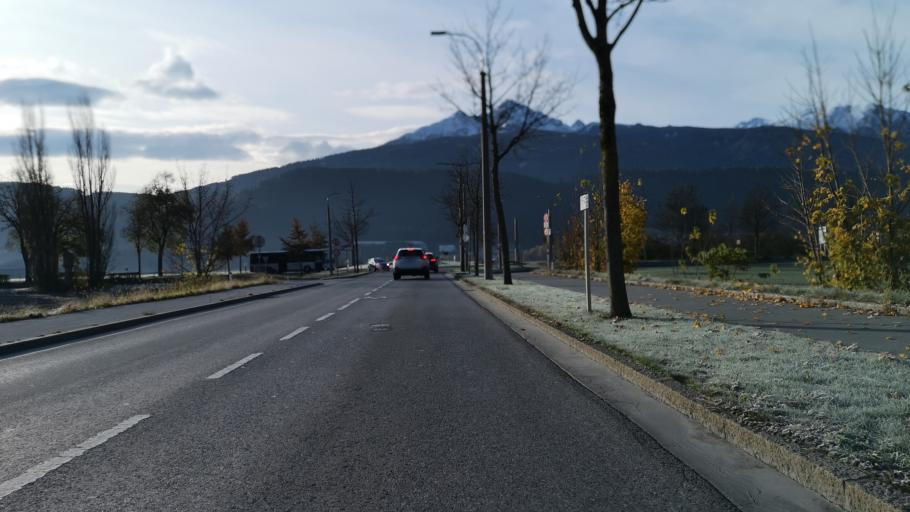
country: AT
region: Tyrol
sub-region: Politischer Bezirk Innsbruck Land
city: Vols
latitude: 47.2632
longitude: 11.3394
